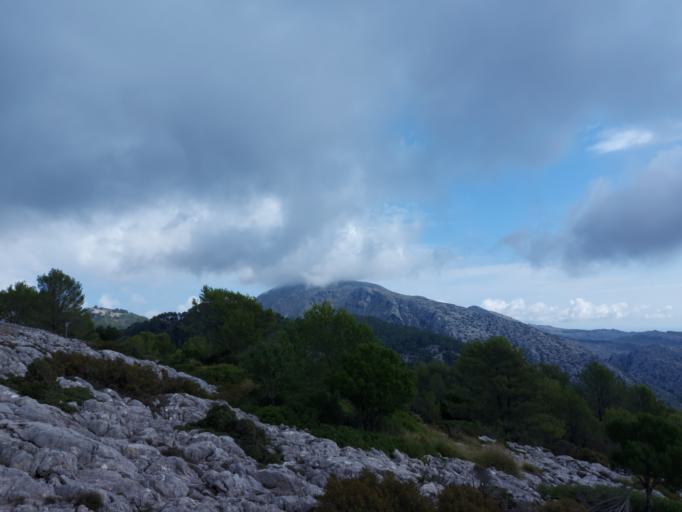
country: ES
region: Balearic Islands
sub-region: Illes Balears
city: Escorca
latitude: 39.8149
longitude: 2.9042
